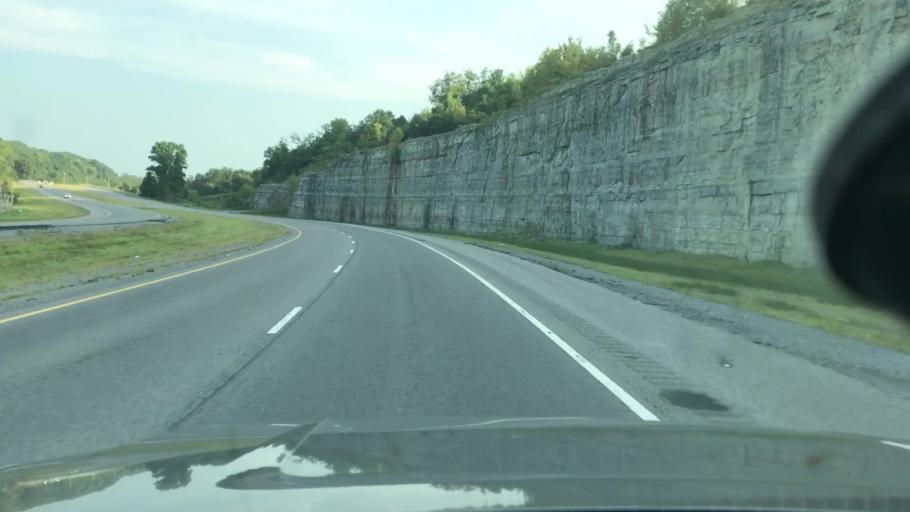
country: US
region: Tennessee
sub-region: Sumner County
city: Gallatin
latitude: 36.4499
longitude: -86.4662
